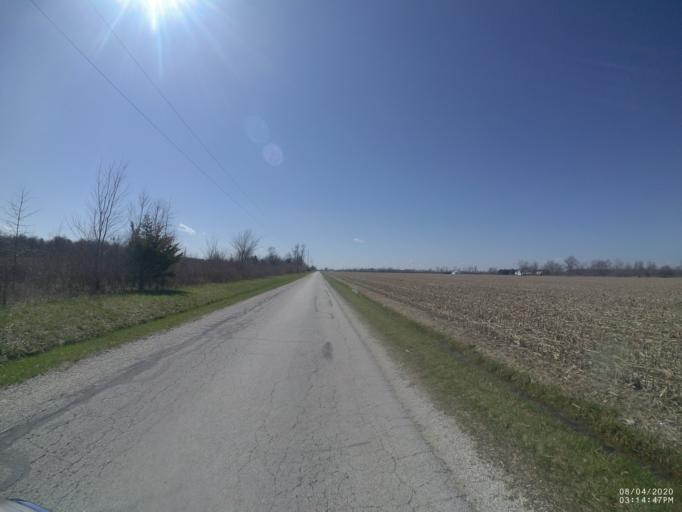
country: US
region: Ohio
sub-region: Sandusky County
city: Stony Prairie
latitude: 41.2829
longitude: -83.2086
